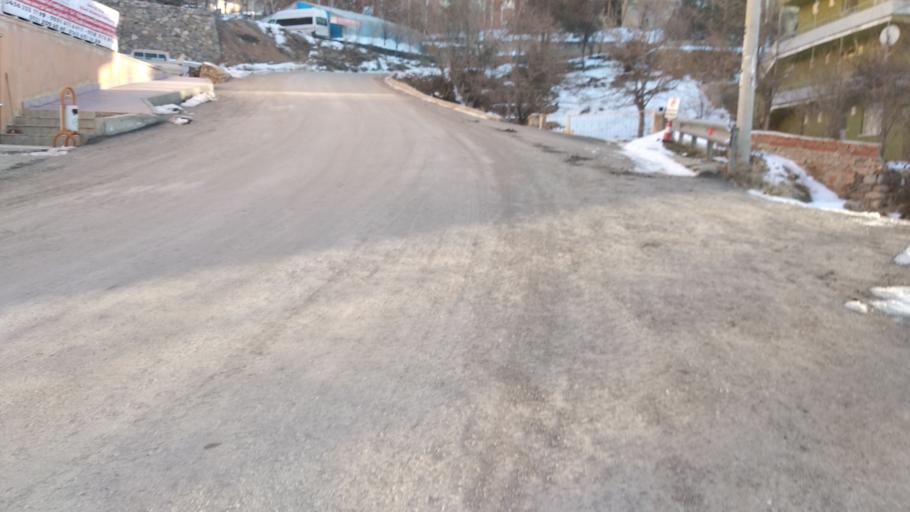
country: TR
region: Gumushane
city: Gumushkhane
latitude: 40.4379
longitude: 39.5076
